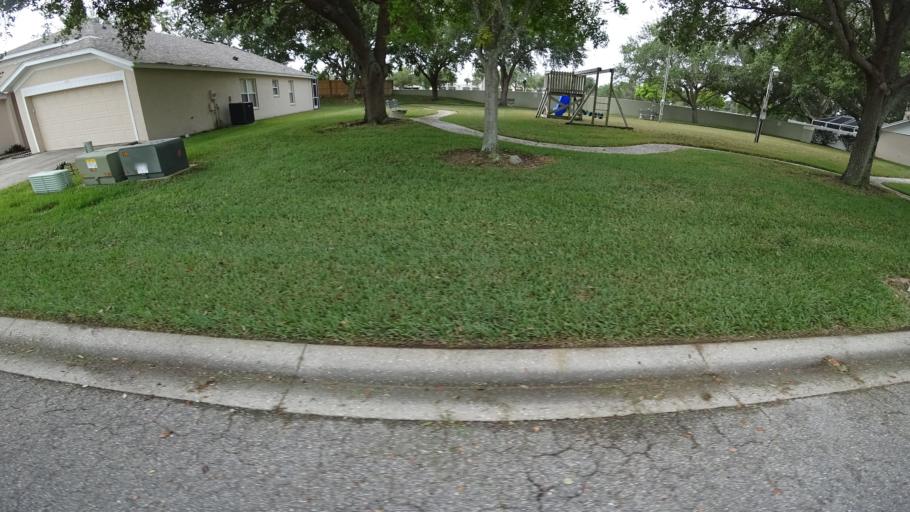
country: US
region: Florida
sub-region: Manatee County
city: South Bradenton
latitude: 27.4485
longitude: -82.6009
